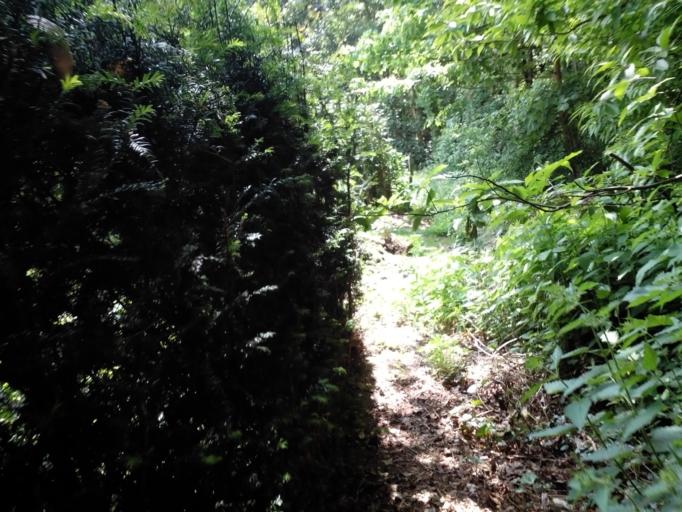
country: BE
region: Flanders
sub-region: Provincie Vlaams-Brabant
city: Holsbeek
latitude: 50.9179
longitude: 4.7562
